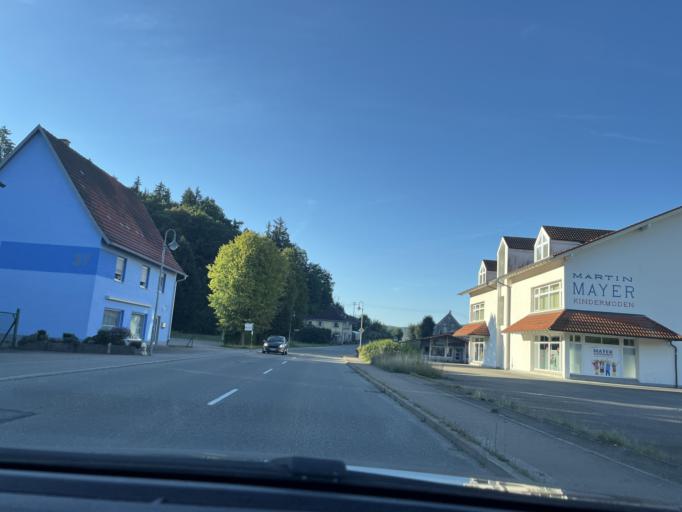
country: DE
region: Baden-Wuerttemberg
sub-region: Tuebingen Region
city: Neufra
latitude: 48.2732
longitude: 9.1688
